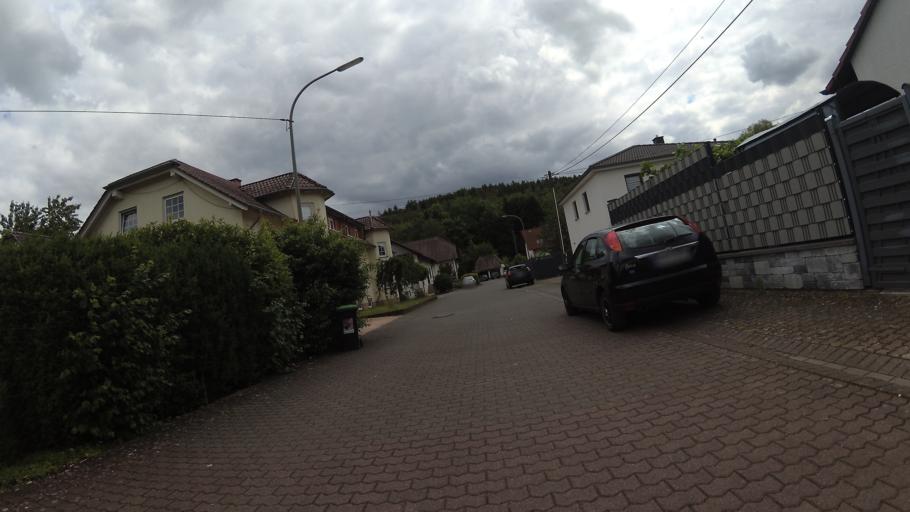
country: DE
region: Saarland
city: Saarwellingen
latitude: 49.3812
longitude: 6.8119
